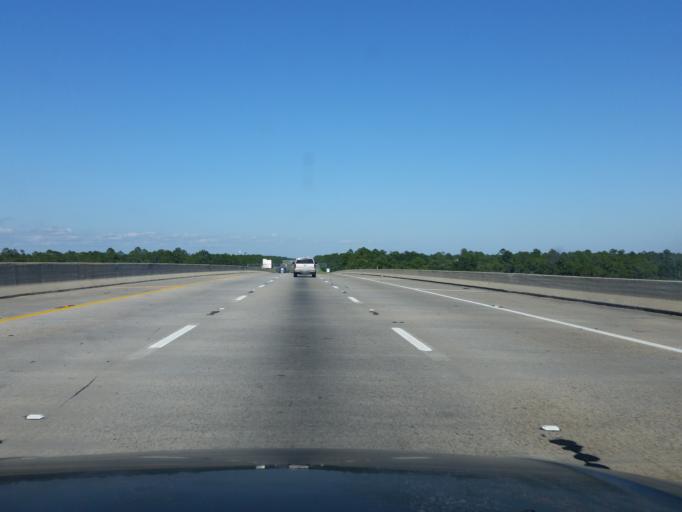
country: US
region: Mississippi
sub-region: Hancock County
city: Diamondhead
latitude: 30.3650
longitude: -89.4013
